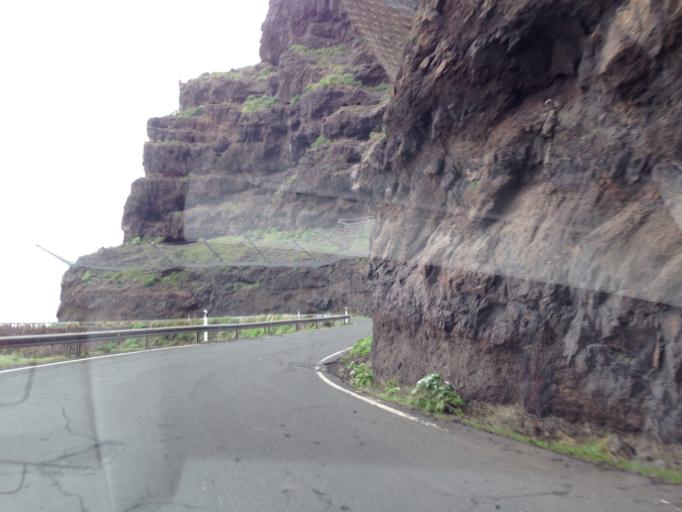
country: ES
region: Canary Islands
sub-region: Provincia de Las Palmas
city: San Nicolas
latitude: 28.0327
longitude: -15.7610
